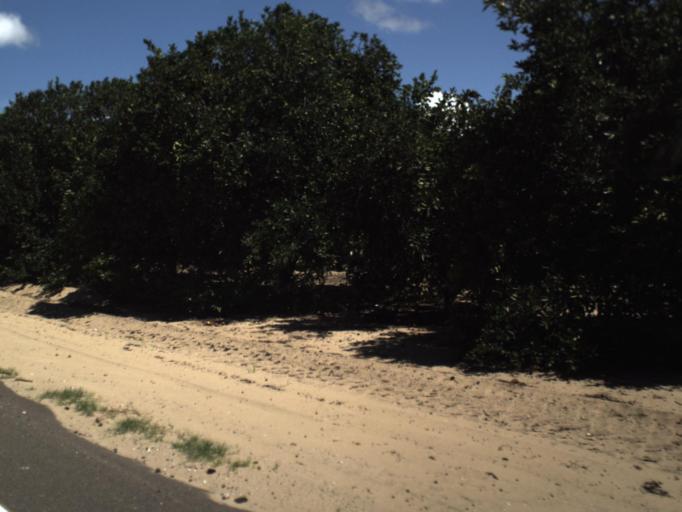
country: US
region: Florida
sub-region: Polk County
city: Babson Park
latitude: 27.7982
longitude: -81.5389
